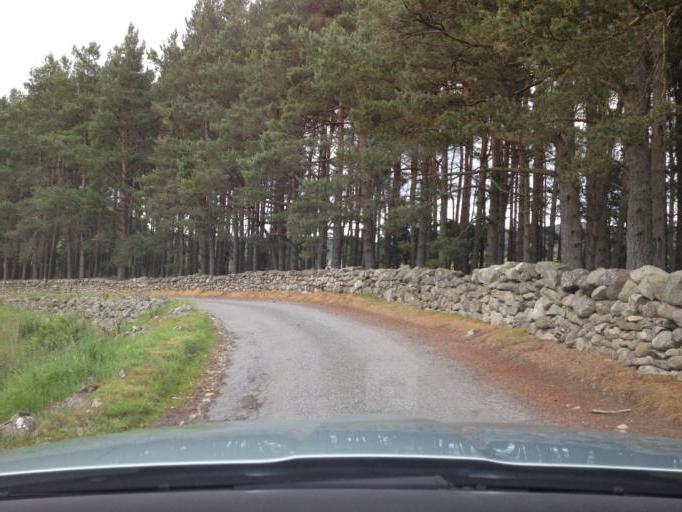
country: GB
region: Scotland
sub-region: Aberdeenshire
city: Aboyne
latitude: 56.9018
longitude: -2.7596
